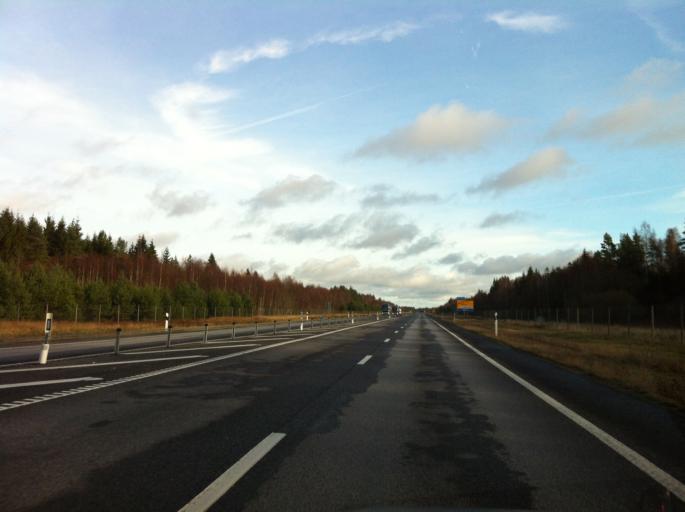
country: SE
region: Kronoberg
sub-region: Alvesta Kommun
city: Vislanda
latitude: 56.6669
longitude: 14.3066
